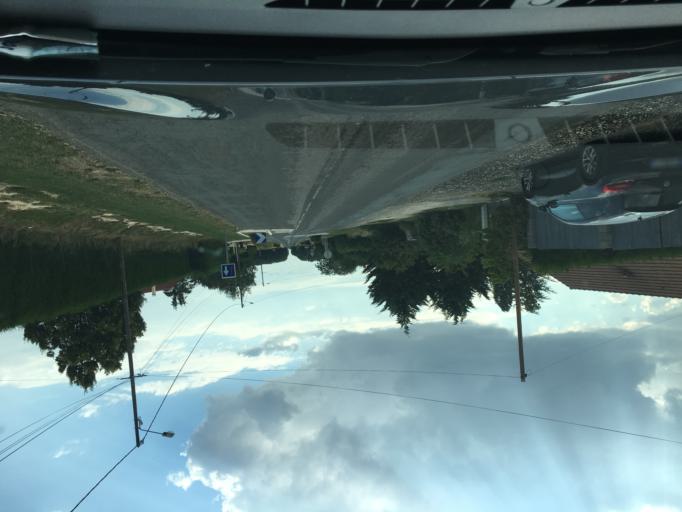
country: FR
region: Centre
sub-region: Departement du Cher
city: Baugy
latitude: 47.0992
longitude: 2.6695
